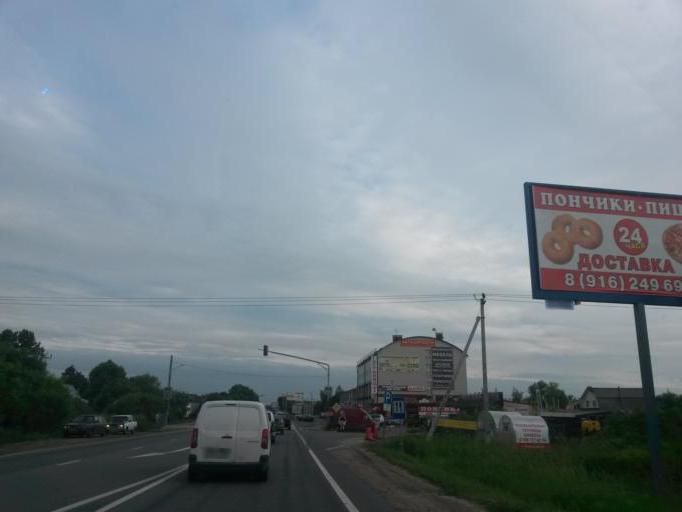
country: RU
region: Moskovskaya
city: Belyye Stolby
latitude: 55.3156
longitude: 37.8106
